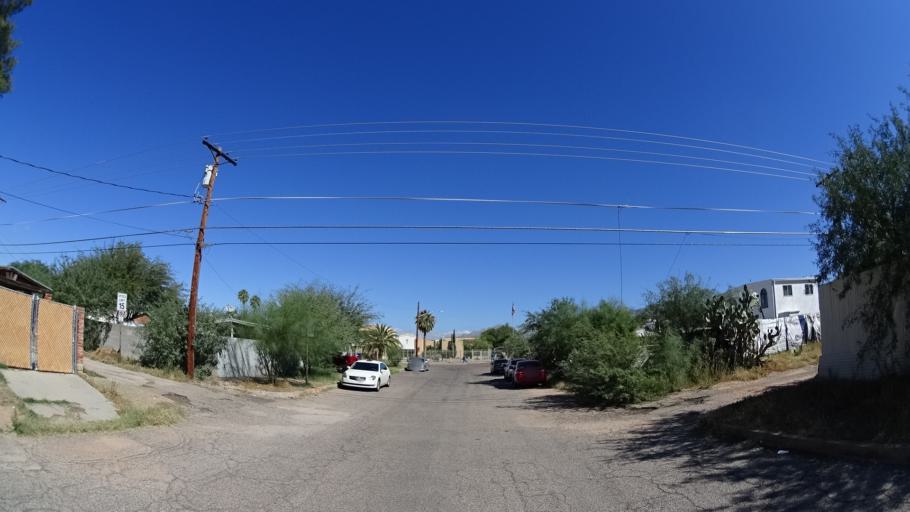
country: US
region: Arizona
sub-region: Pima County
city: Tucson
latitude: 32.2534
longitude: -110.9498
